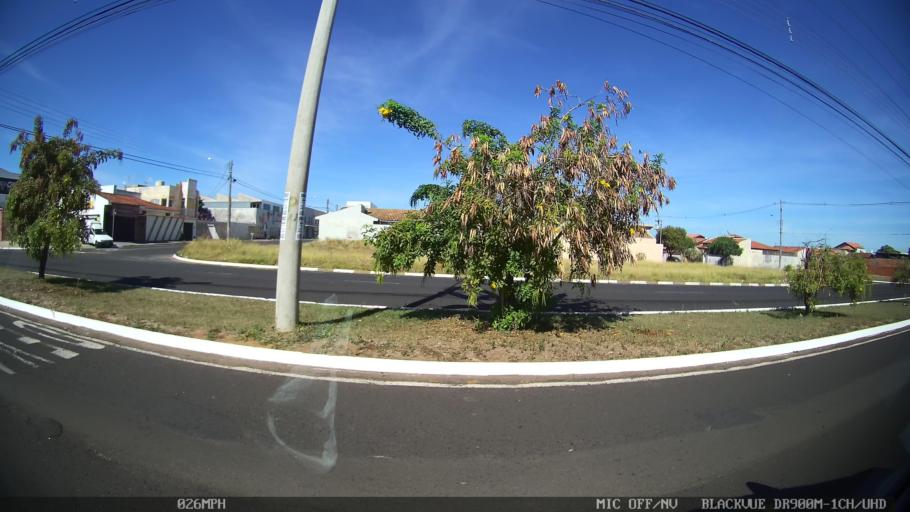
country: BR
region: Sao Paulo
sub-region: Franca
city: Franca
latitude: -20.5423
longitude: -47.3774
